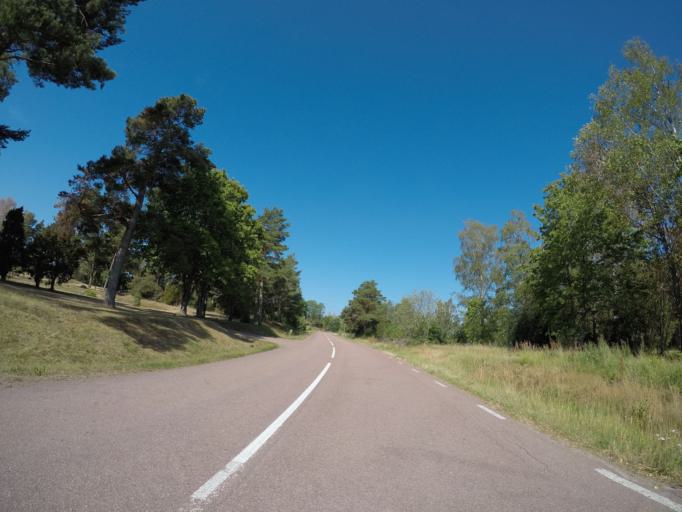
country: AX
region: Alands landsbygd
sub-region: Finstroem
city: Finstroem
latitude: 60.2754
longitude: 19.9117
